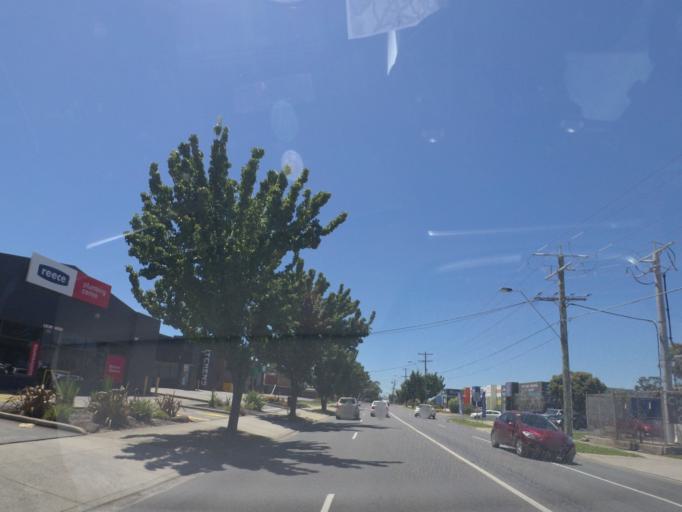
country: AU
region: Victoria
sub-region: Darebin
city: Kingsbury
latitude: -37.6944
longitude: 145.0394
